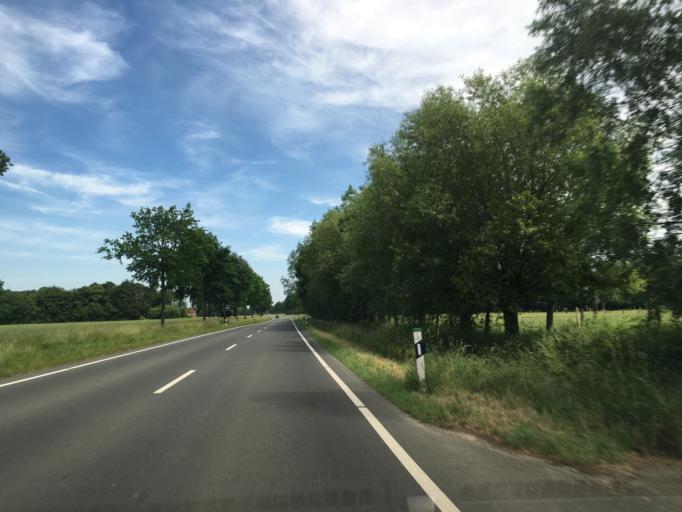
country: DE
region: North Rhine-Westphalia
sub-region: Regierungsbezirk Munster
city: Nordwalde
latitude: 52.0647
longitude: 7.5240
